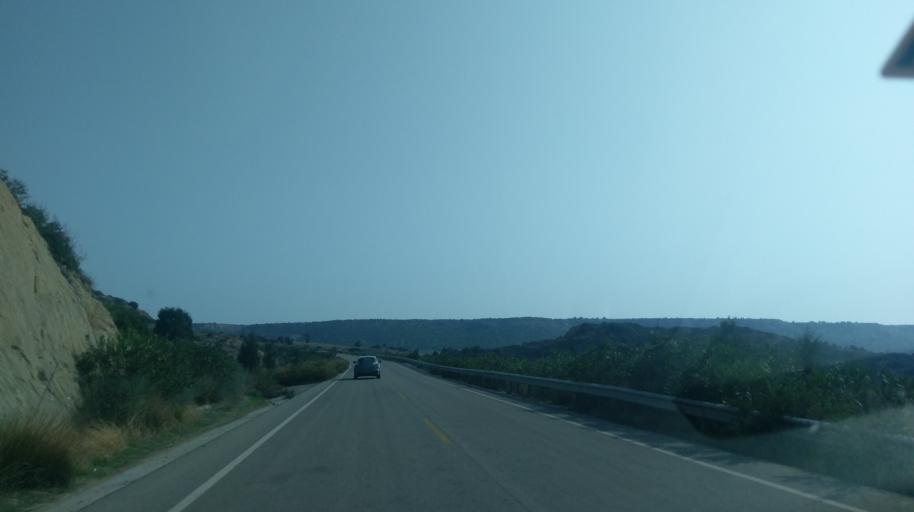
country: CY
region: Ammochostos
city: Leonarisso
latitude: 35.4784
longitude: 34.1148
